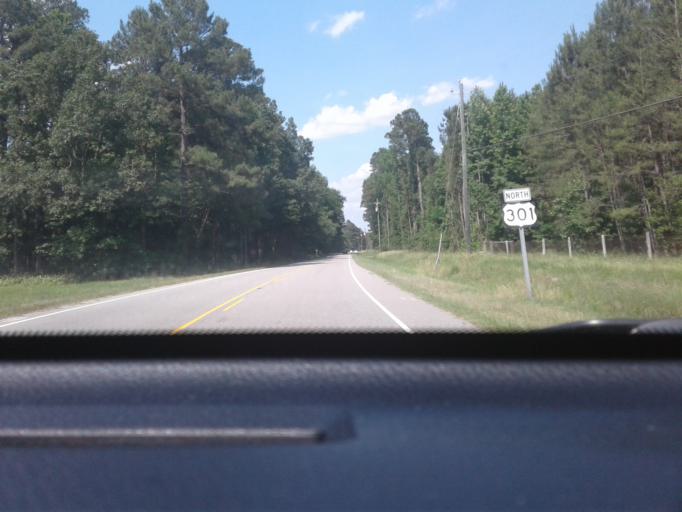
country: US
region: North Carolina
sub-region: Cumberland County
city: Eastover
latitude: 35.1730
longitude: -78.7215
